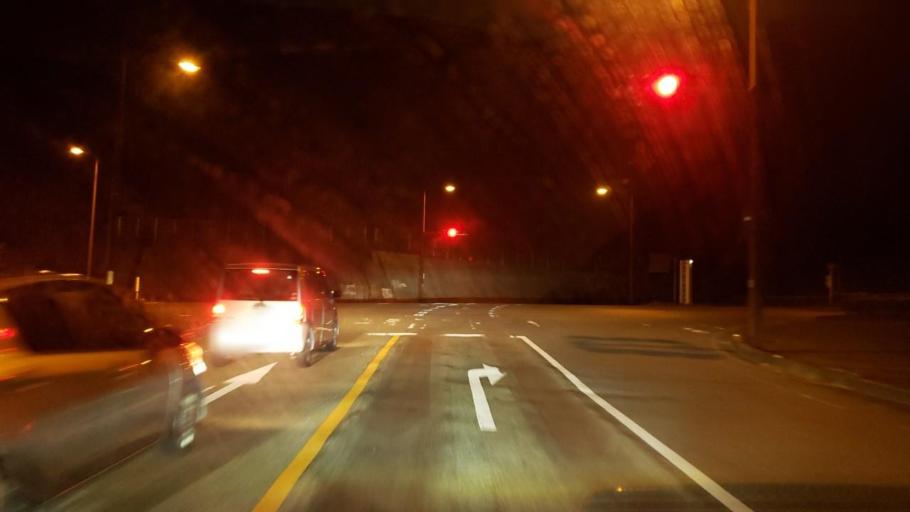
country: JP
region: Tokushima
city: Narutocho-mitsuishi
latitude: 34.1975
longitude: 134.5873
